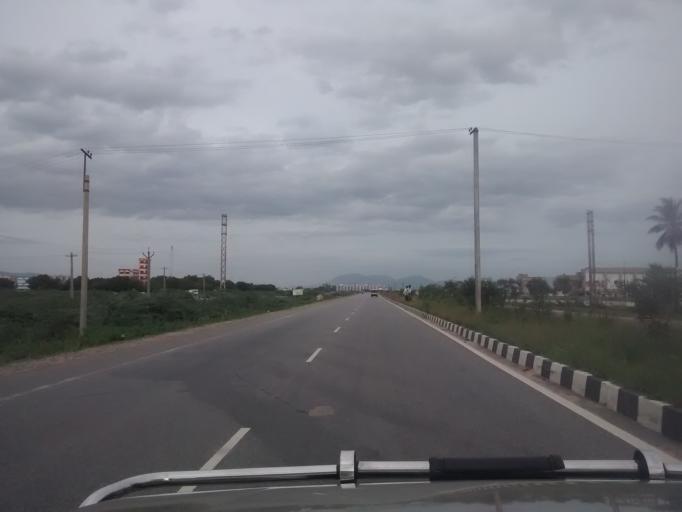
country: IN
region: Andhra Pradesh
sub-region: Chittoor
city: Tirupati
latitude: 13.6048
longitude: 79.3972
